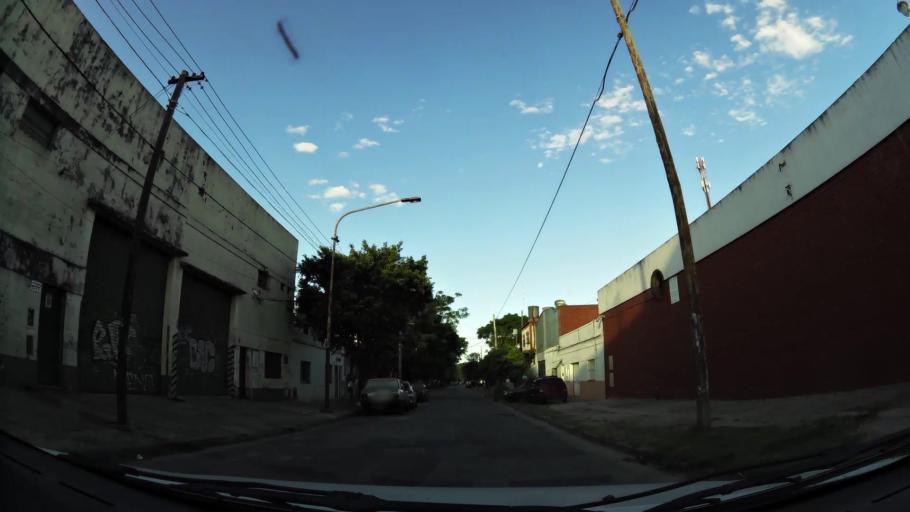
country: AR
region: Buenos Aires
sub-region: Partido de General San Martin
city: General San Martin
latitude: -34.5656
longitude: -58.5214
